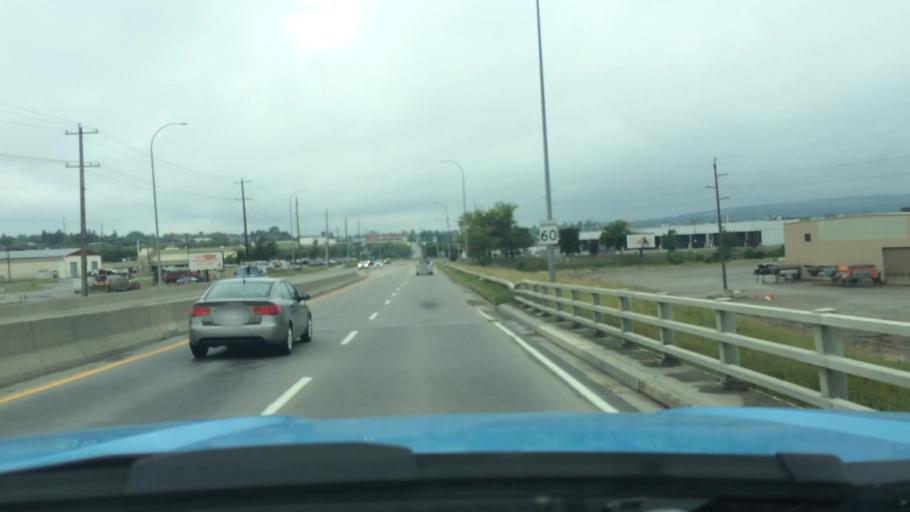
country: CA
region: Alberta
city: Calgary
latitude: 51.0816
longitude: -114.0384
